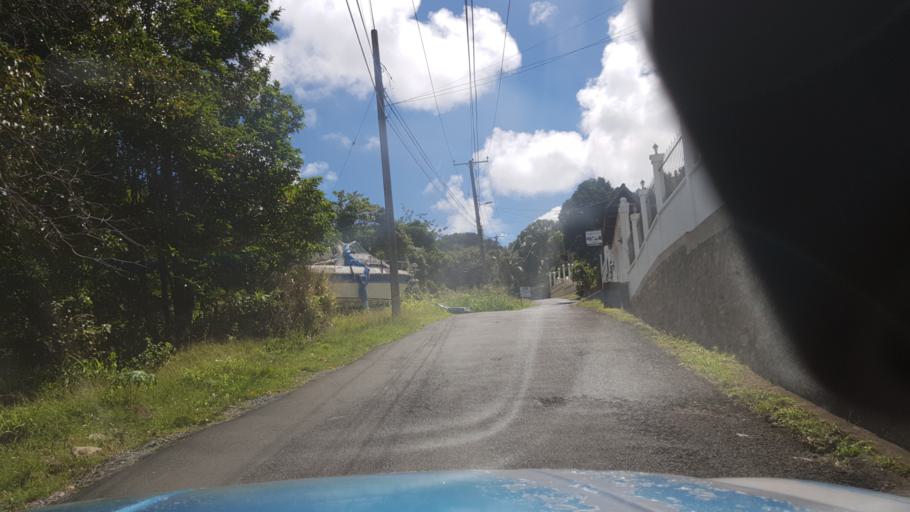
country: LC
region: Gros-Islet
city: Gros Islet
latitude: 14.0452
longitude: -60.9535
